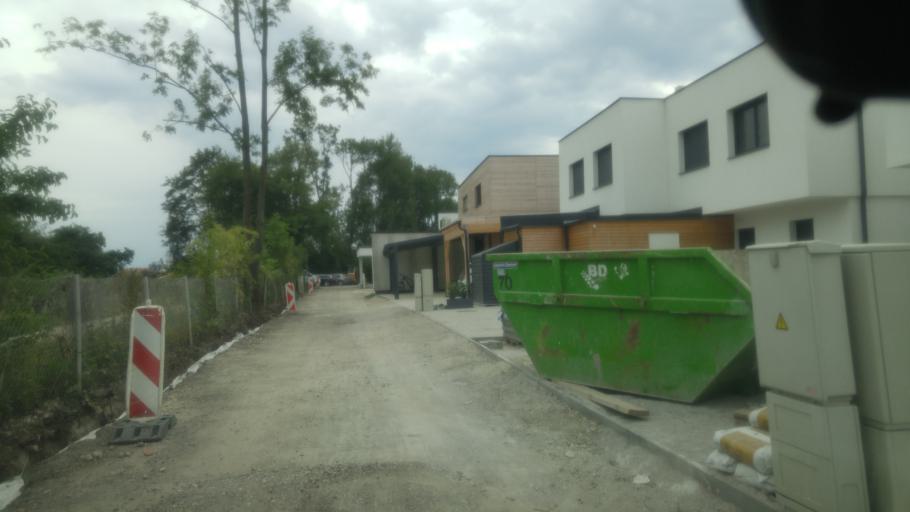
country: AT
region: Lower Austria
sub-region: Politischer Bezirk Wien-Umgebung
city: Moosbrunn
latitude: 48.0411
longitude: 16.4397
